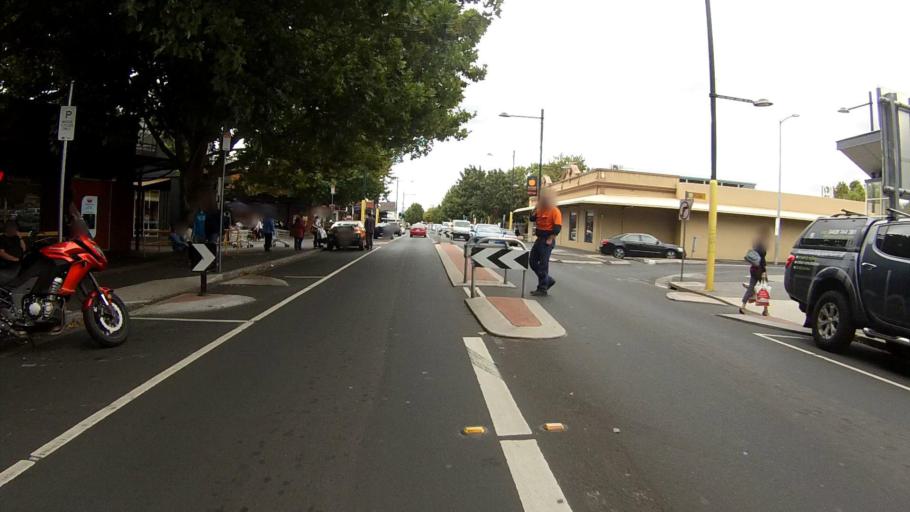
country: AU
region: Tasmania
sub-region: Glenorchy
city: Glenorchy
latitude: -42.8326
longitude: 147.2732
